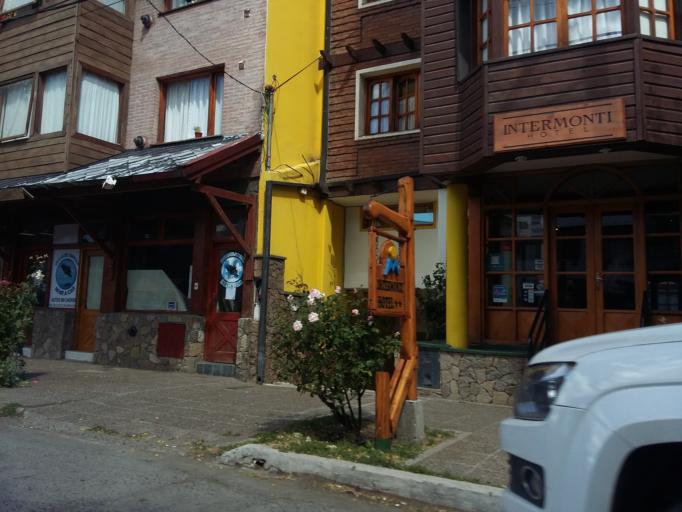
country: AR
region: Neuquen
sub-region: Departamento de Lacar
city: San Martin de los Andes
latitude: -40.1584
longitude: -71.3515
